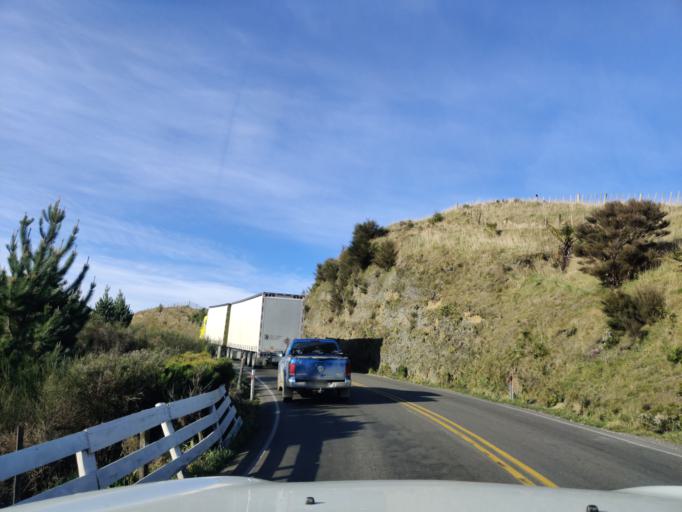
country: NZ
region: Manawatu-Wanganui
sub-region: Palmerston North City
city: Palmerston North
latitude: -40.2894
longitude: 175.7965
